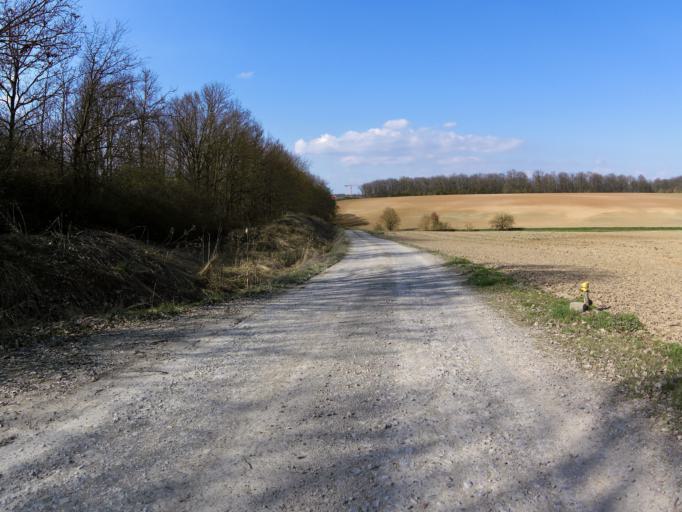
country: DE
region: Bavaria
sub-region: Regierungsbezirk Unterfranken
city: Rottendorf
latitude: 49.7979
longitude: 10.0529
